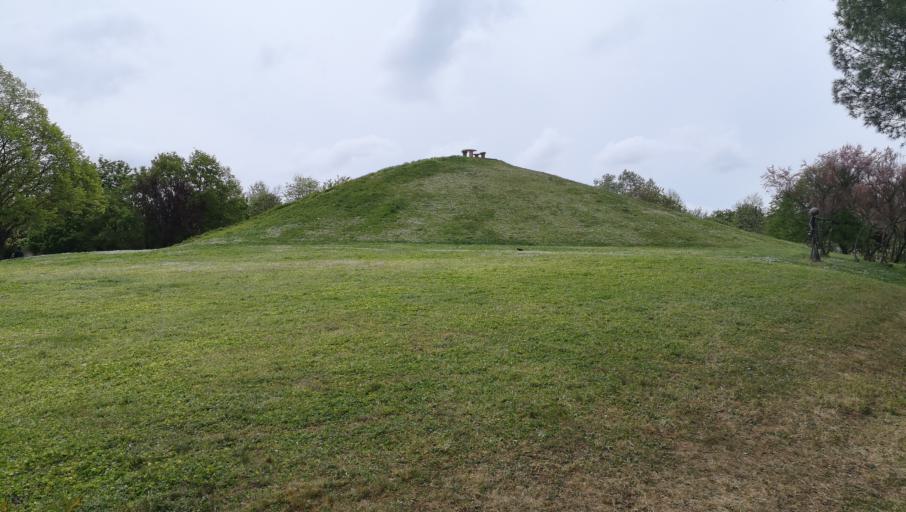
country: FR
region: Midi-Pyrenees
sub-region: Departement de la Haute-Garonne
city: Blagnac
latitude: 43.6339
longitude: 1.3835
